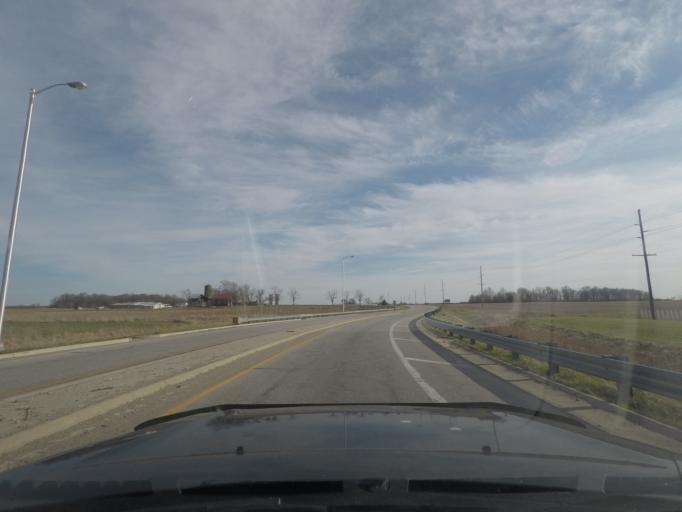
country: US
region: Indiana
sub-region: Elkhart County
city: Wakarusa
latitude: 41.5071
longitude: -86.0021
